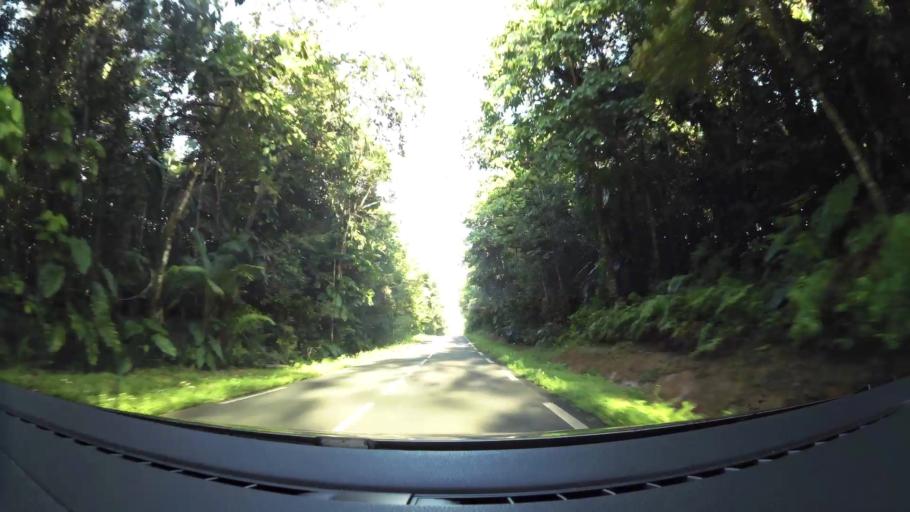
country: GP
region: Guadeloupe
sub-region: Guadeloupe
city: Bouillante
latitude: 16.1798
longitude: -61.6872
